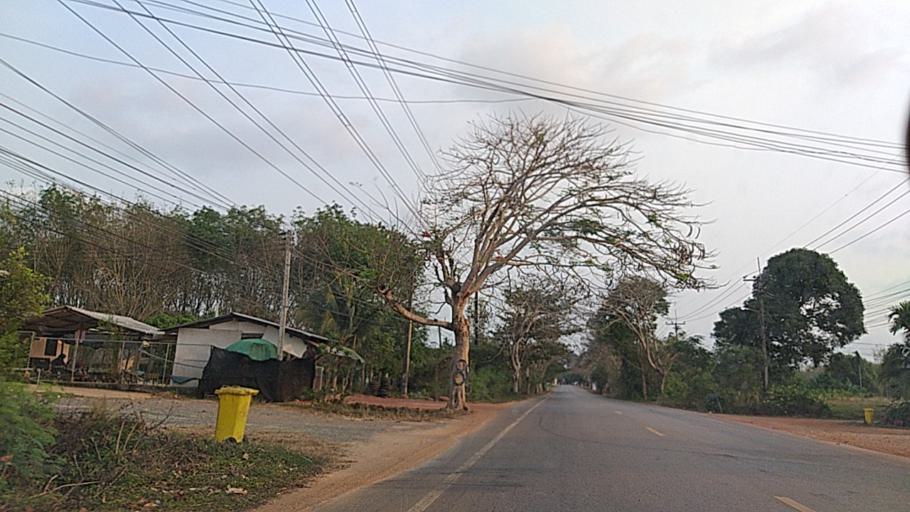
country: TH
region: Trat
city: Laem Ngop
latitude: 12.2464
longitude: 102.2937
